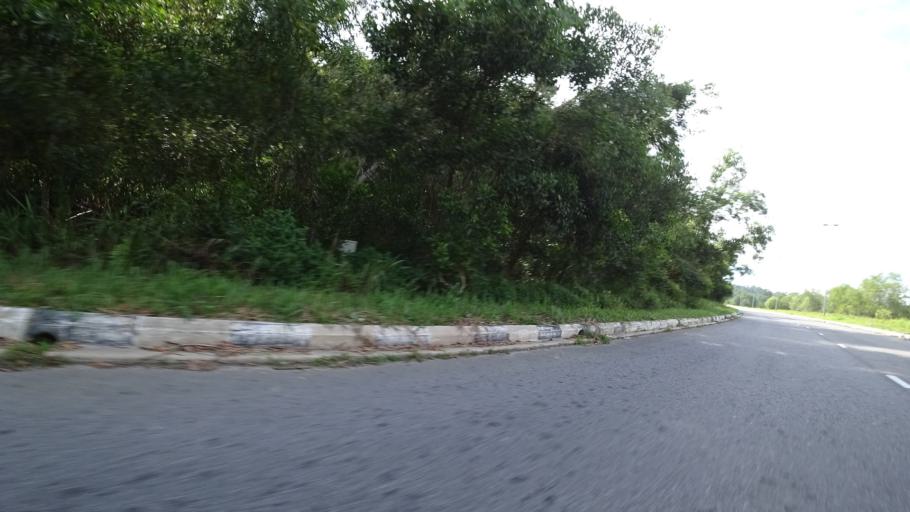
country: BN
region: Brunei and Muara
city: Bandar Seri Begawan
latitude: 4.9000
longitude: 114.8017
